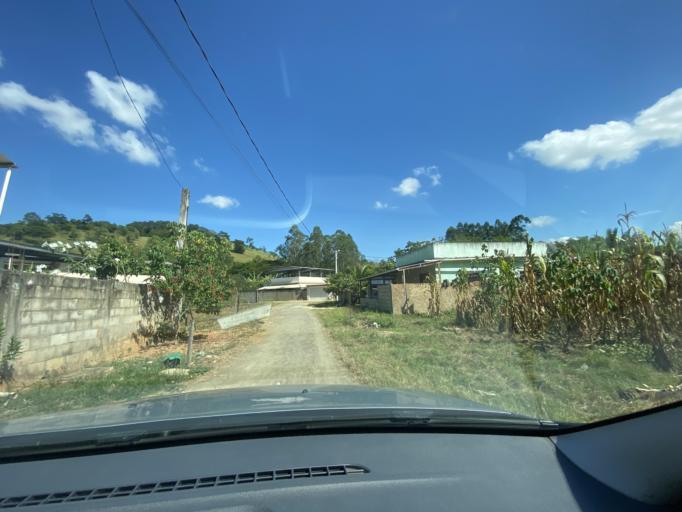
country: BR
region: Espirito Santo
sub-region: Jeronimo Monteiro
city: Jeronimo Monteiro
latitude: -20.7976
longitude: -41.4057
